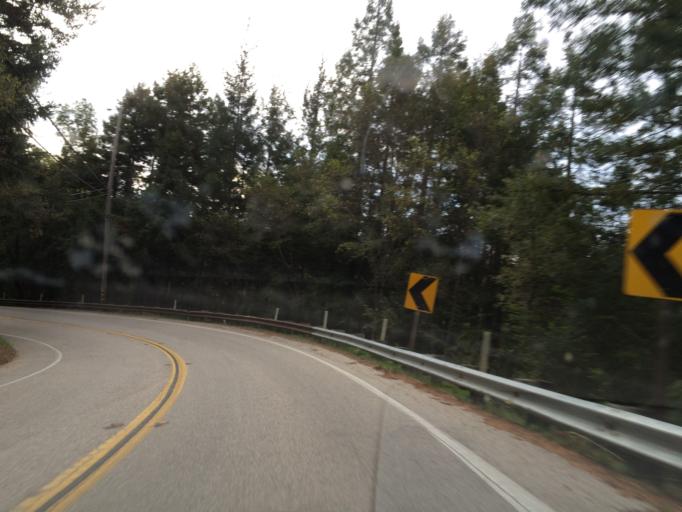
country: US
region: California
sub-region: Santa Cruz County
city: Felton
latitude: 37.0388
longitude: -122.1077
